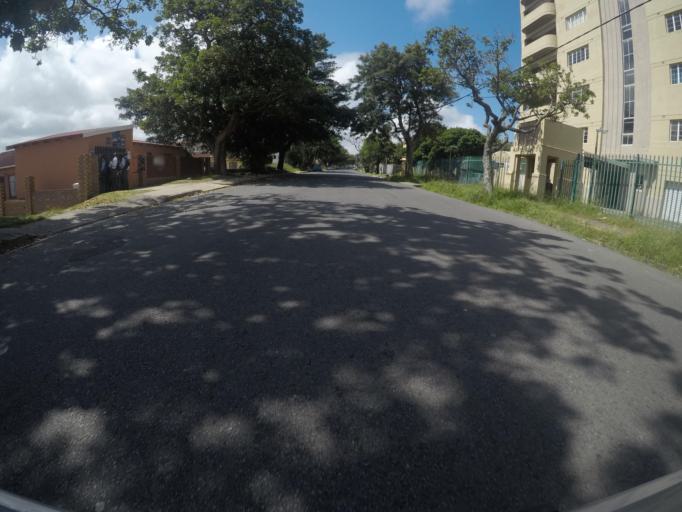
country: ZA
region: Eastern Cape
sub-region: Buffalo City Metropolitan Municipality
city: East London
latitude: -33.0003
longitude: 27.8959
